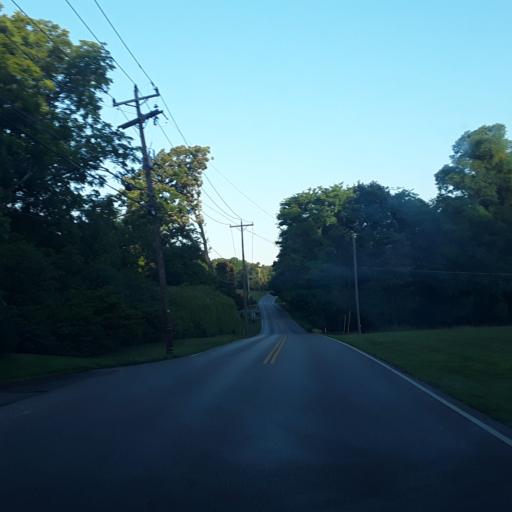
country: US
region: Tennessee
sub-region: Davidson County
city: Oak Hill
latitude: 36.0778
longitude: -86.7791
